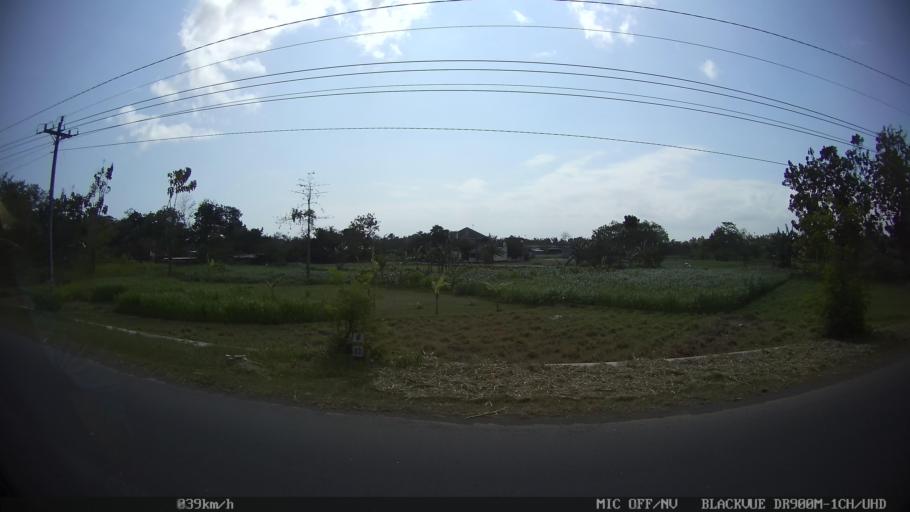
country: ID
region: Daerah Istimewa Yogyakarta
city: Pundong
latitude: -7.9794
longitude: 110.3387
